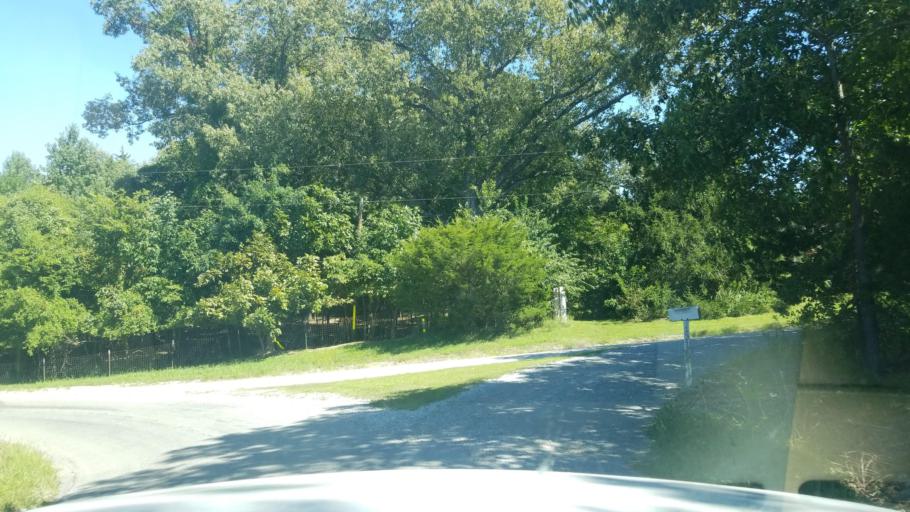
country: US
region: Illinois
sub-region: Saline County
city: Eldorado
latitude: 37.8525
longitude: -88.5122
